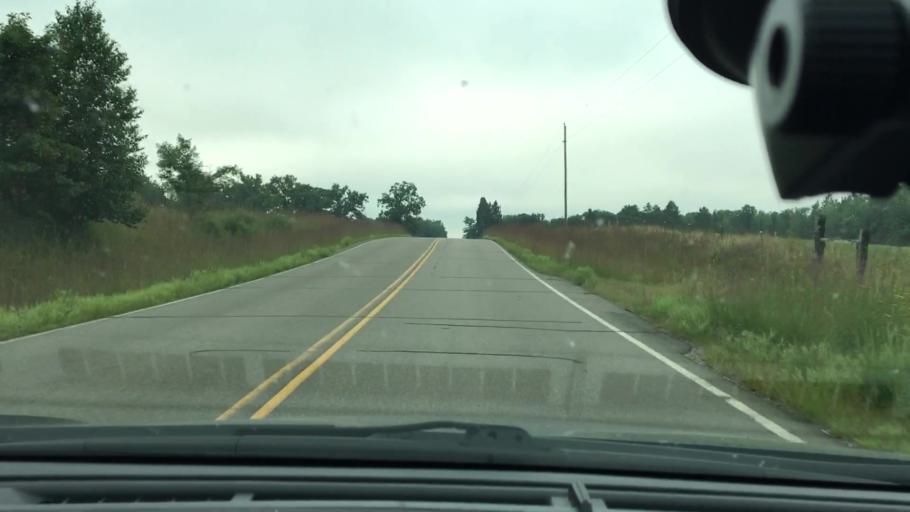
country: US
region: Minnesota
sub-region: Crow Wing County
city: Cross Lake
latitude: 46.6472
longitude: -94.0096
